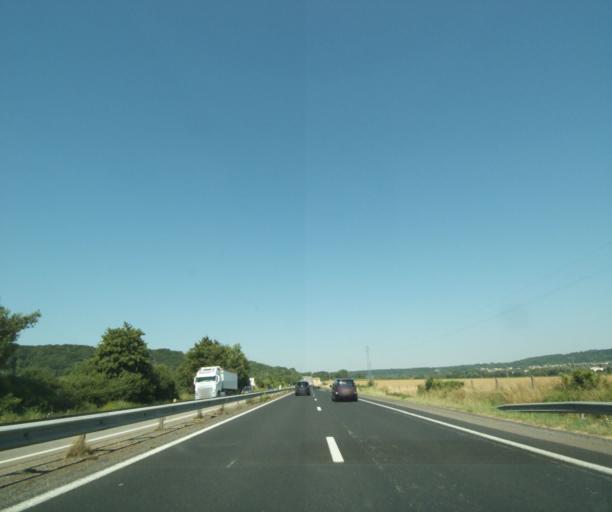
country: FR
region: Lorraine
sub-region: Departement de Meurthe-et-Moselle
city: Domgermain
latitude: 48.6677
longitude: 5.8195
